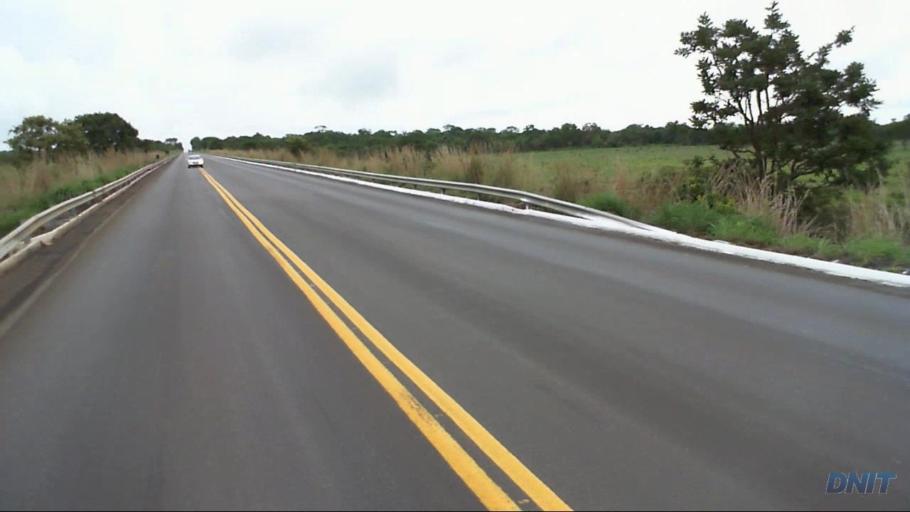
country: BR
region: Goias
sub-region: Padre Bernardo
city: Padre Bernardo
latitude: -15.1764
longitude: -48.4083
